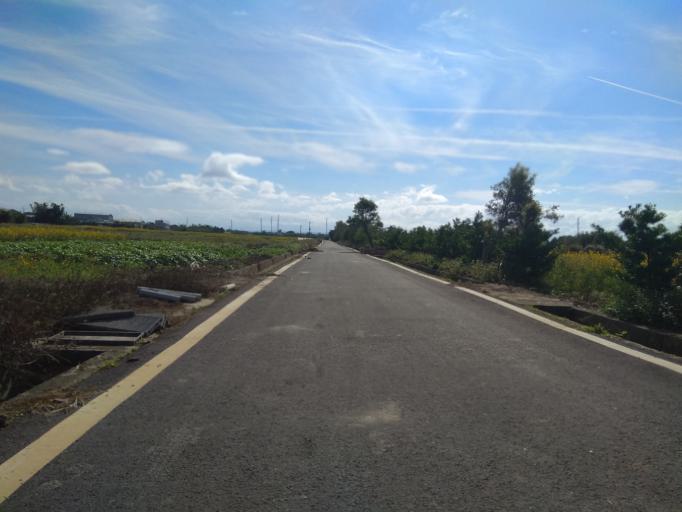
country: TW
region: Taiwan
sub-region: Hsinchu
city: Zhubei
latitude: 24.9977
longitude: 121.0393
